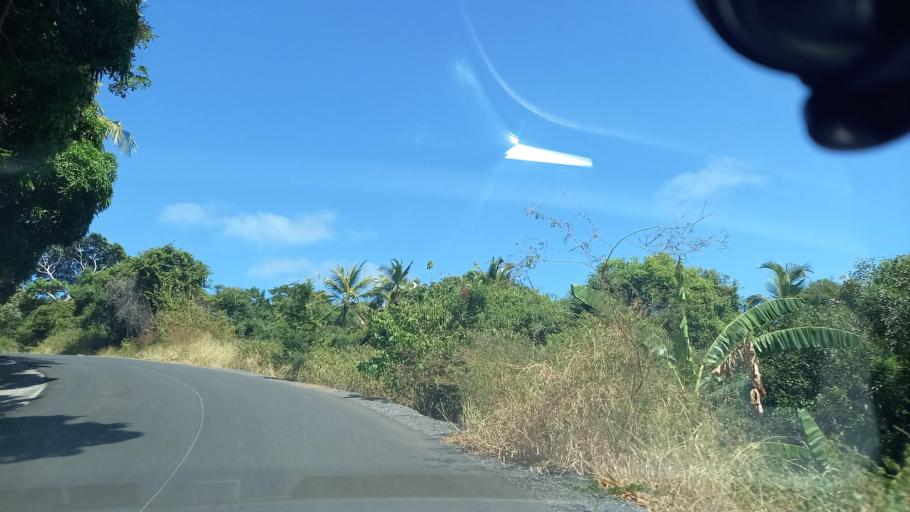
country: YT
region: Kani-Keli
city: Kani Keli
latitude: -12.9681
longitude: 45.1113
